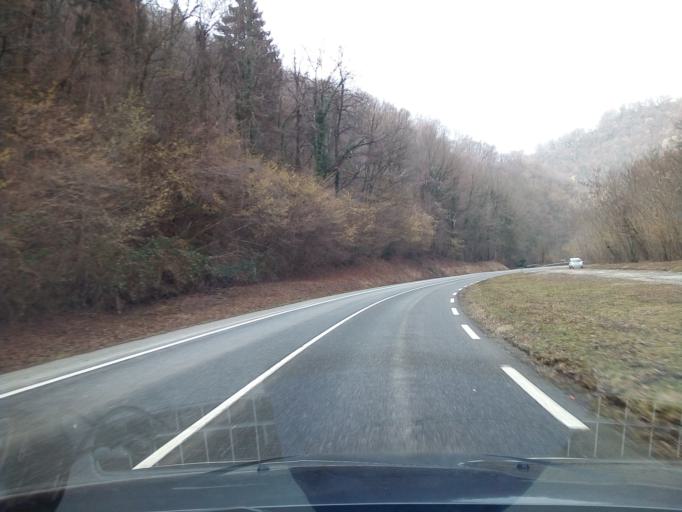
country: FR
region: Rhone-Alpes
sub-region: Departement de l'Isere
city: Gieres
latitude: 45.1659
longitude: 5.7991
